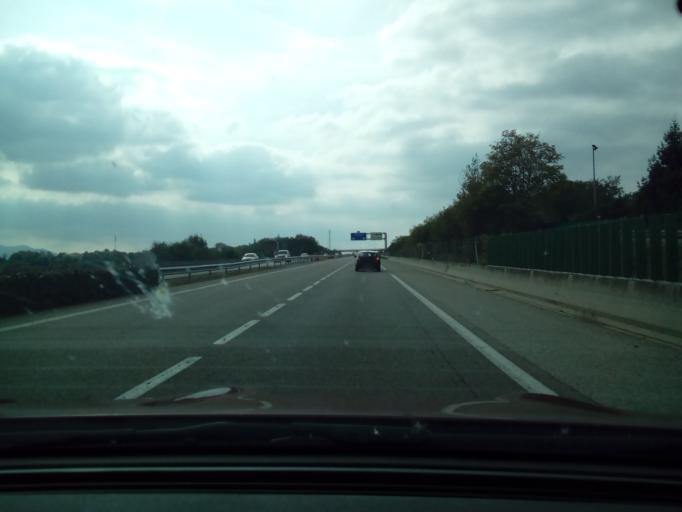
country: FR
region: Rhone-Alpes
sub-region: Departement de l'Isere
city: Saint-Marcellin
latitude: 45.1381
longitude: 5.3303
